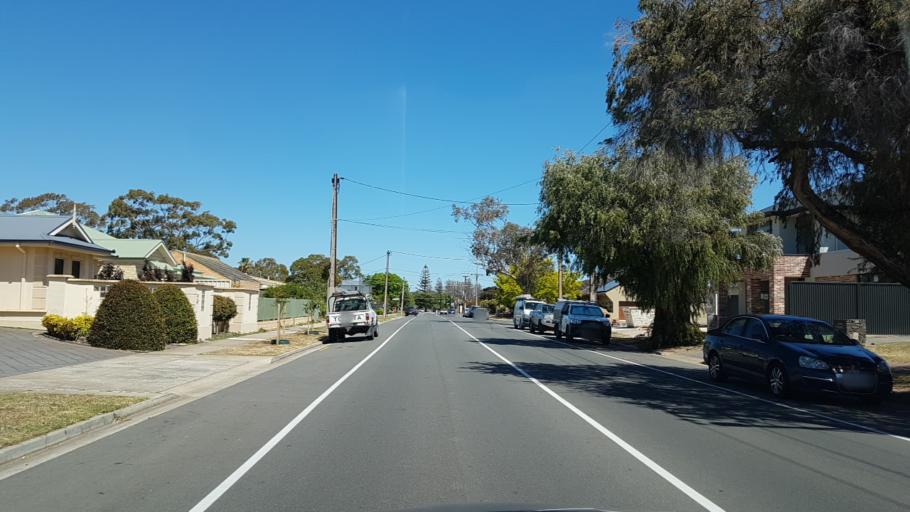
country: AU
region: South Australia
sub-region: Holdfast Bay
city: Glenelg East
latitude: -34.9720
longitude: 138.5285
